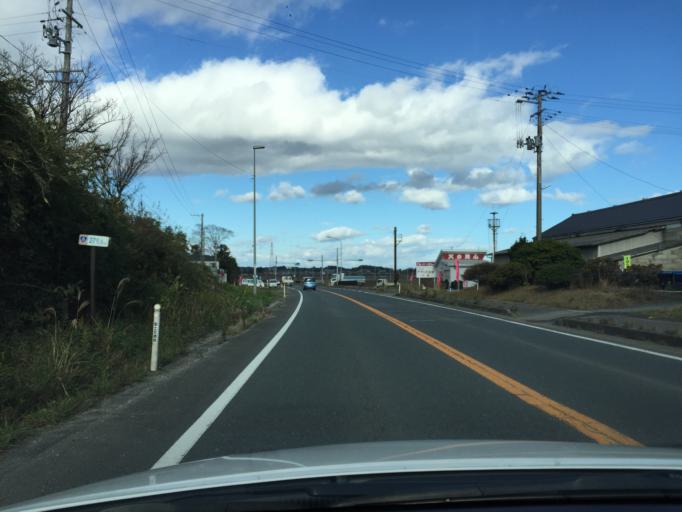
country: JP
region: Fukushima
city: Namie
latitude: 37.5845
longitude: 141.0090
